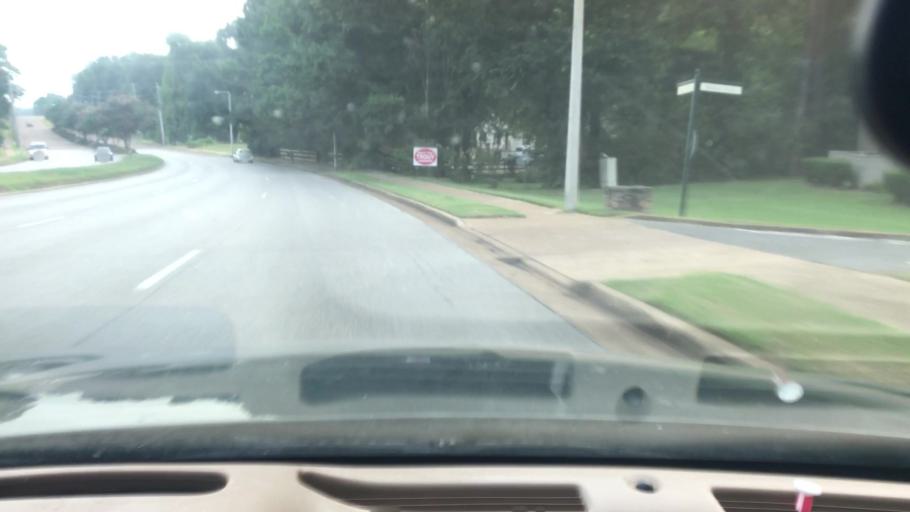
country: US
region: Tennessee
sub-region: Shelby County
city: Bartlett
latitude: 35.1862
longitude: -89.8696
